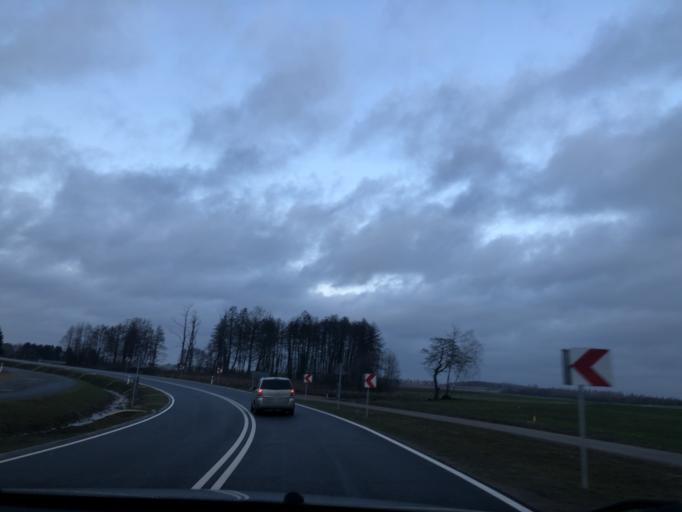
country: PL
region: Podlasie
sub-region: Lomza
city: Lomza
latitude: 53.1259
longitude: 22.0485
